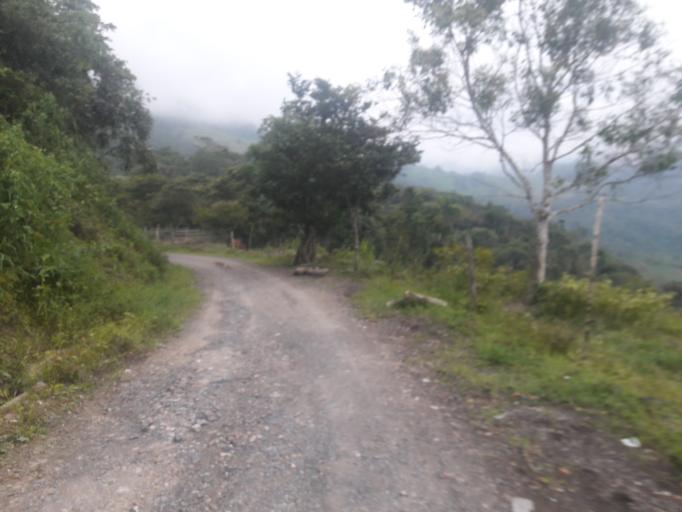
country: CO
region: Boyaca
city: Otanche
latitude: 5.5868
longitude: -74.2256
